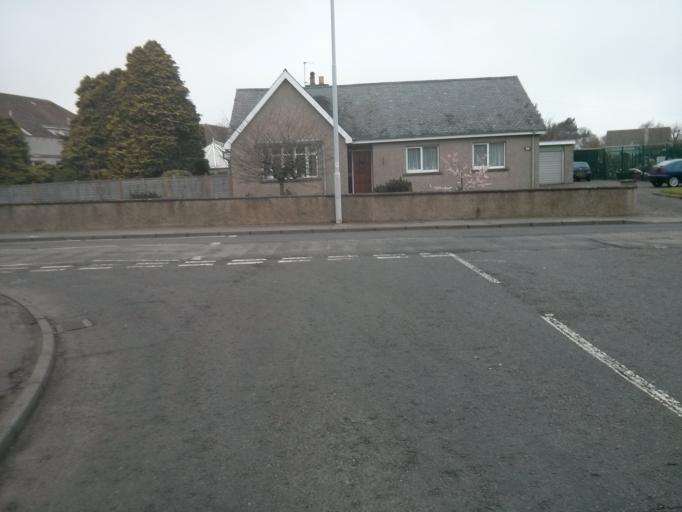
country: GB
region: Scotland
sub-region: Fife
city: Saint Andrews
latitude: 56.3292
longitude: -2.8055
